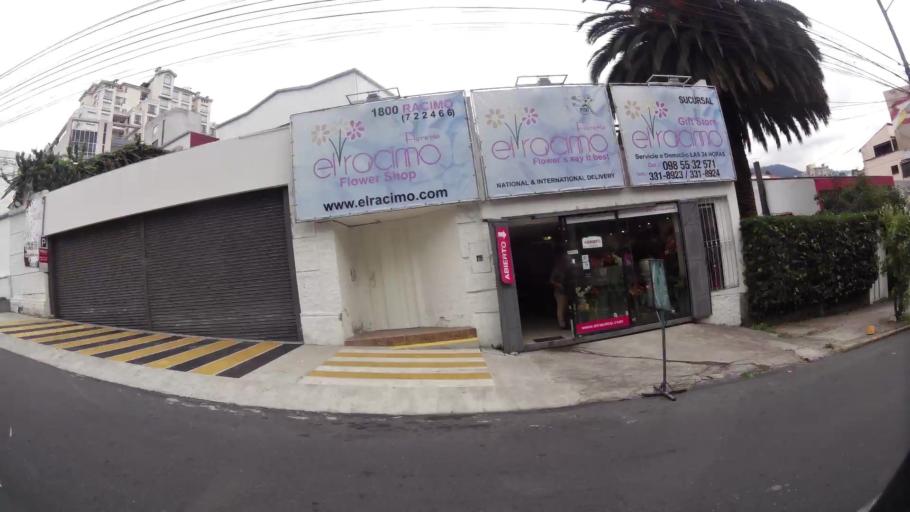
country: EC
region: Pichincha
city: Quito
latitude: -0.1650
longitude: -78.4894
